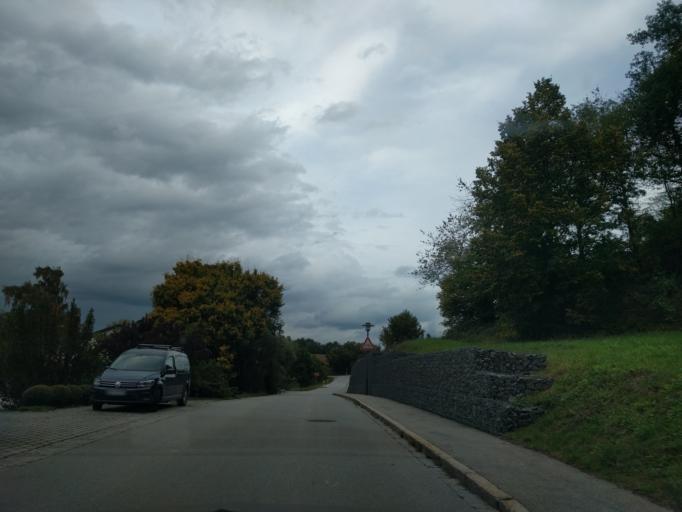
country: DE
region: Bavaria
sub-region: Lower Bavaria
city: Winzer
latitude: 48.7277
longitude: 13.0741
